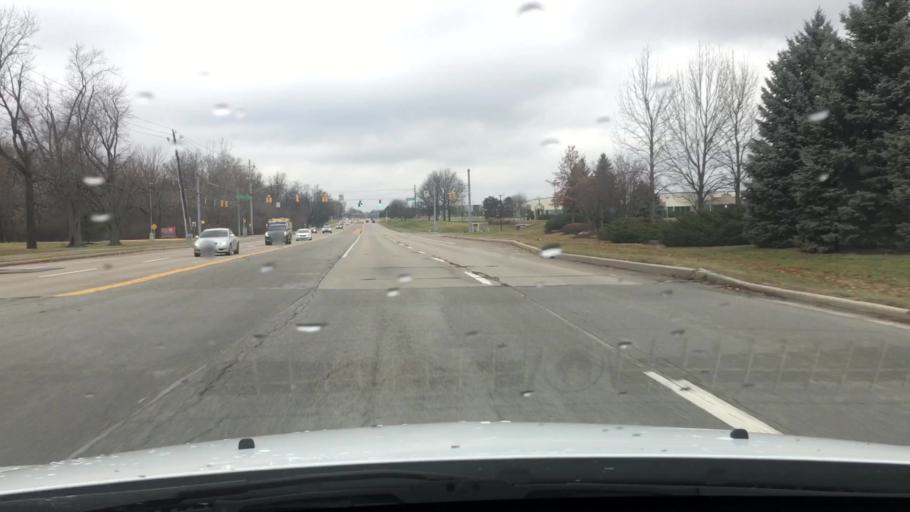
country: US
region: Indiana
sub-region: Boone County
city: Zionsville
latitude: 39.8819
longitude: -86.2512
